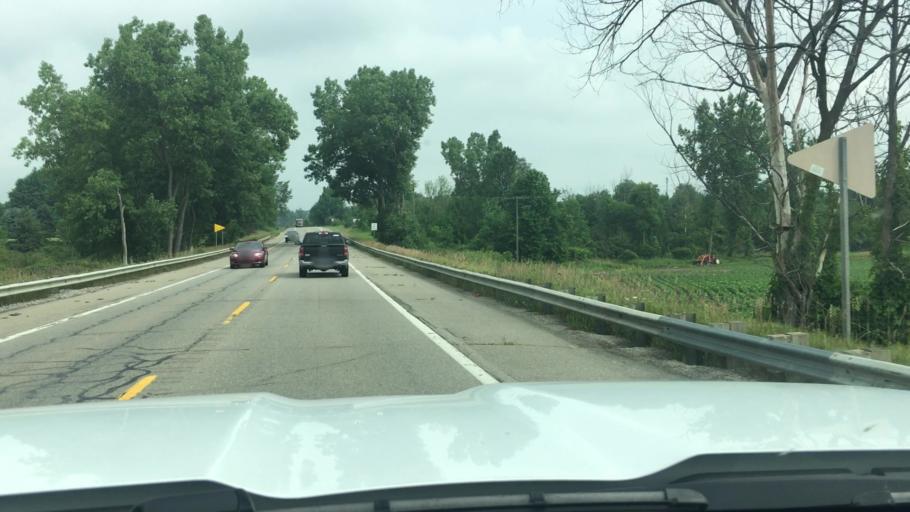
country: US
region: Michigan
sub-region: Sanilac County
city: Brown City
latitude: 43.1439
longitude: -83.0741
